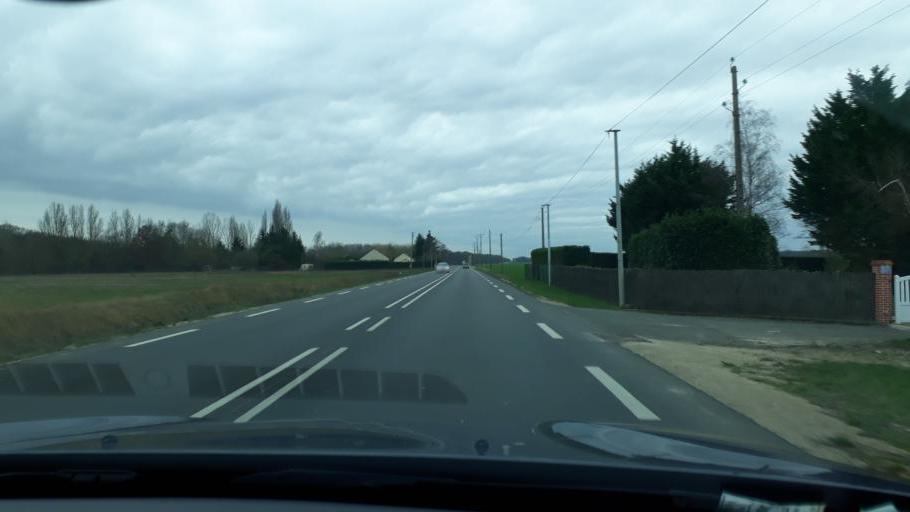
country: FR
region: Centre
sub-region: Departement du Loiret
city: Chanteau
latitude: 48.0321
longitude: 1.9744
